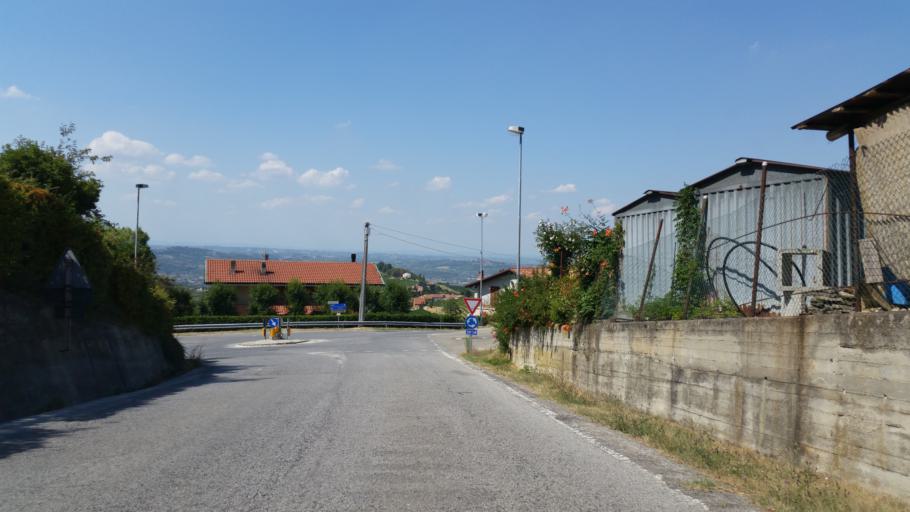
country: IT
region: Piedmont
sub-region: Provincia di Cuneo
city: Treiso
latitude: 44.6894
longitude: 8.0897
